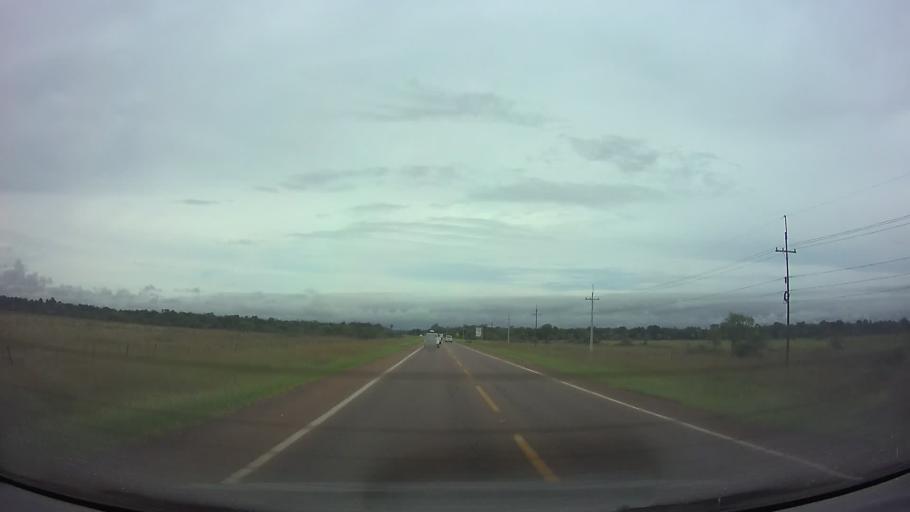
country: PY
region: Paraguari
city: Carapegua
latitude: -25.7314
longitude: -57.2074
